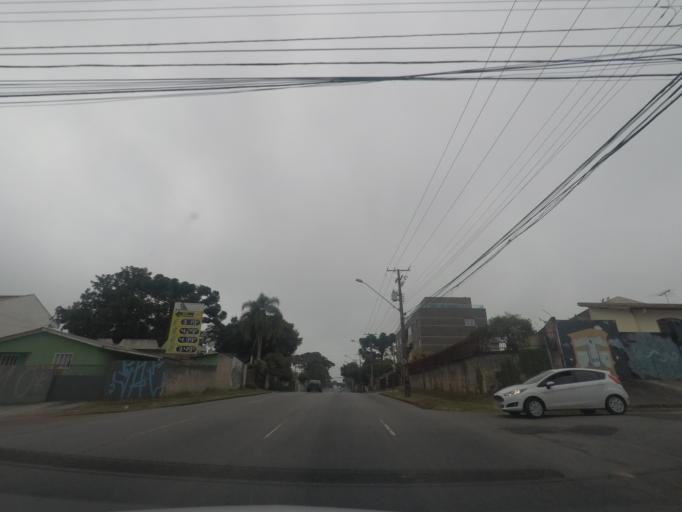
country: BR
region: Parana
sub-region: Curitiba
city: Curitiba
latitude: -25.3805
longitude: -49.2257
